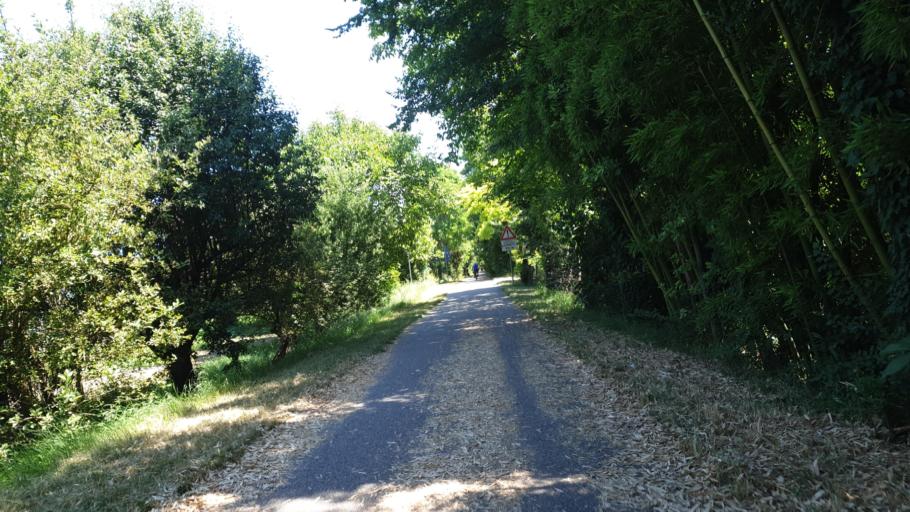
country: IT
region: Veneto
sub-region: Provincia di Padova
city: San Giorgio delle Pertiche
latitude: 45.5557
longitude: 11.9001
